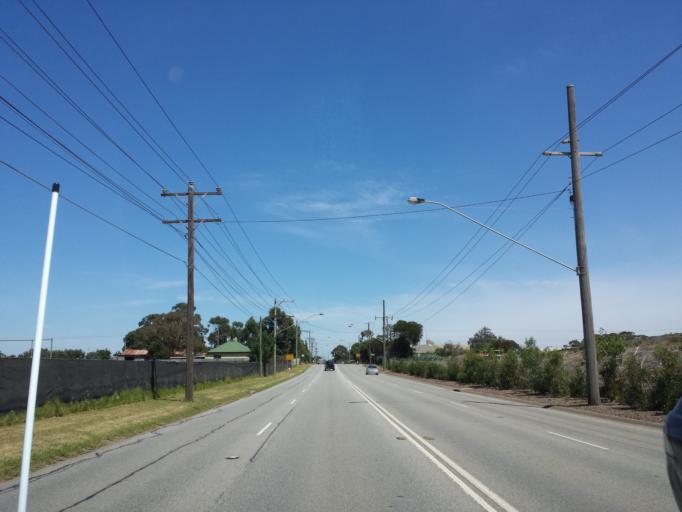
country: AU
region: Victoria
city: Heatherton
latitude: -37.9584
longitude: 145.1199
